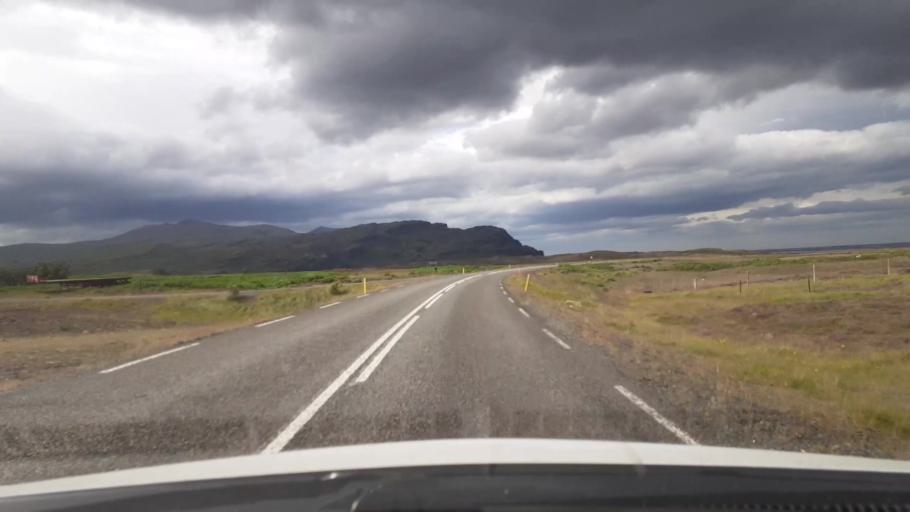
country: IS
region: West
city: Borgarnes
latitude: 64.5449
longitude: -21.6598
